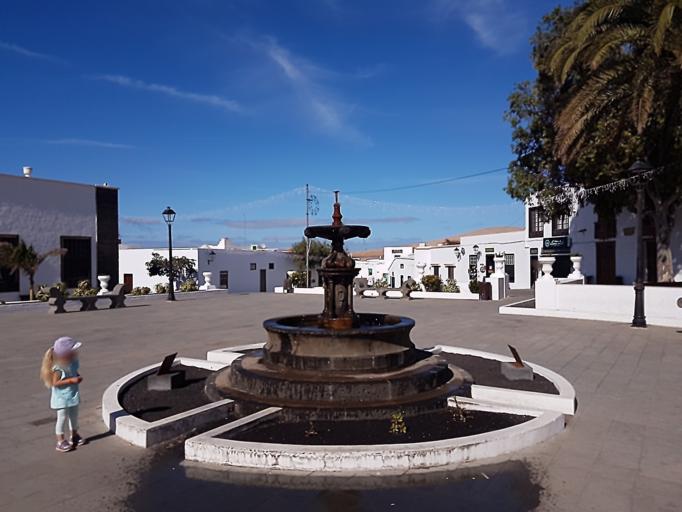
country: ES
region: Canary Islands
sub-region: Provincia de Las Palmas
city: Teguise
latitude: 29.0593
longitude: -13.5600
